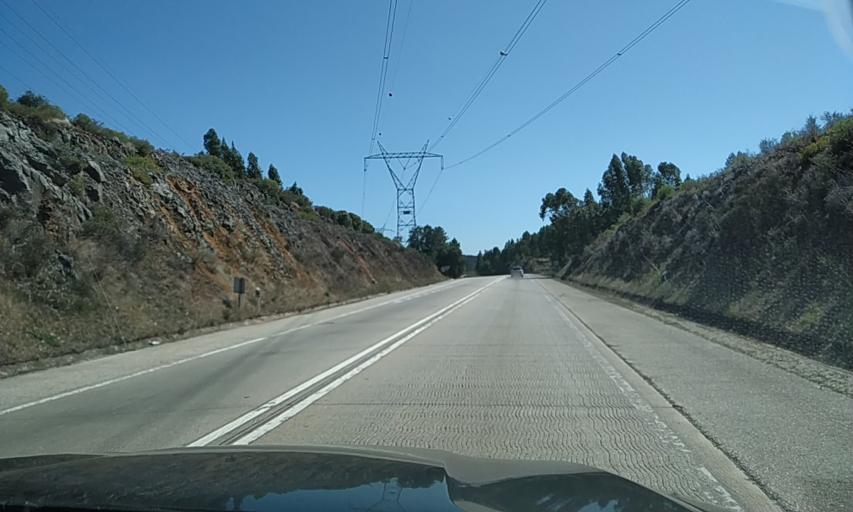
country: PT
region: Santarem
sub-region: Rio Maior
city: Rio Maior
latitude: 39.3542
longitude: -8.9708
